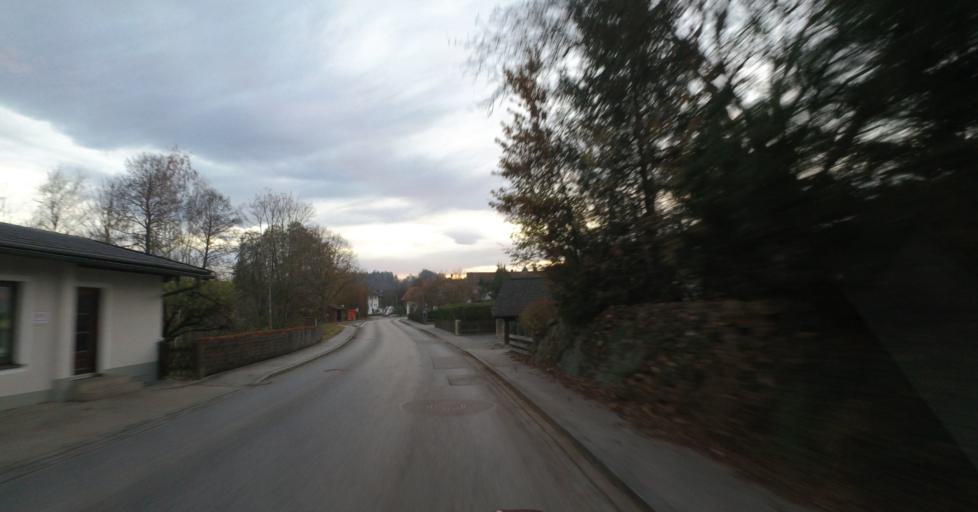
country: DE
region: Bavaria
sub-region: Upper Bavaria
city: Prien am Chiemsee
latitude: 47.8467
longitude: 12.3186
